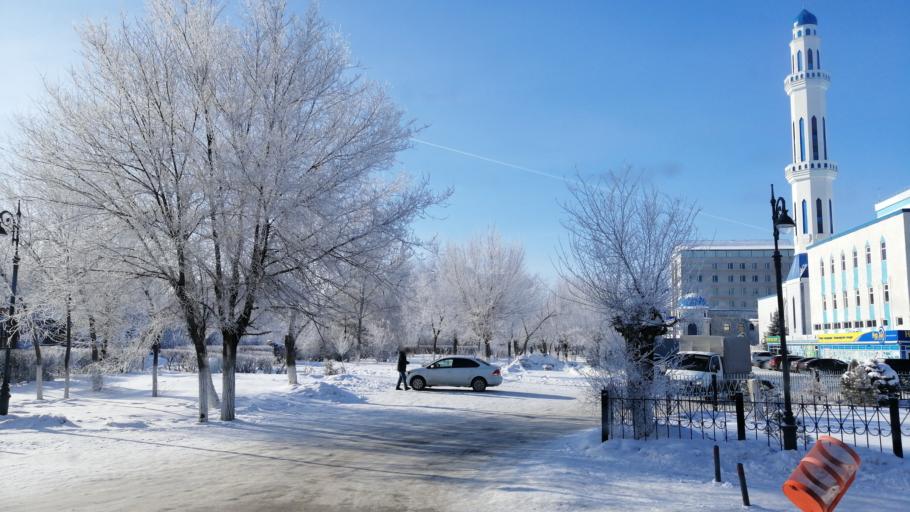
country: KZ
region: Aqtoebe
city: Aqtobe
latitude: 50.2961
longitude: 57.1575
